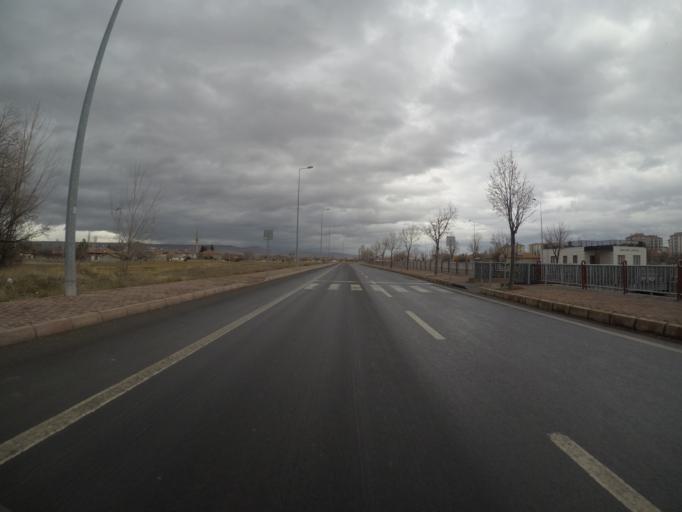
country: TR
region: Kayseri
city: Kayseri
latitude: 38.7533
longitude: 35.4766
